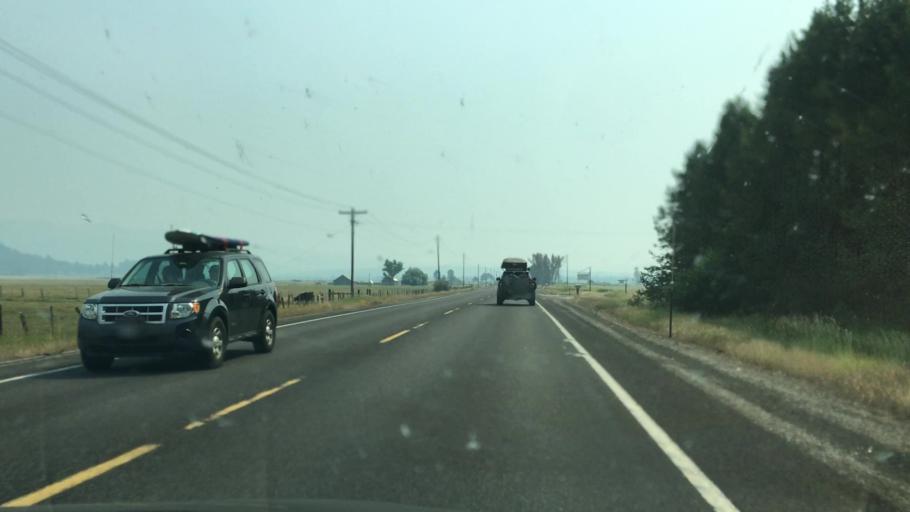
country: US
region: Idaho
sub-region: Valley County
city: Cascade
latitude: 44.4368
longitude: -115.9995
